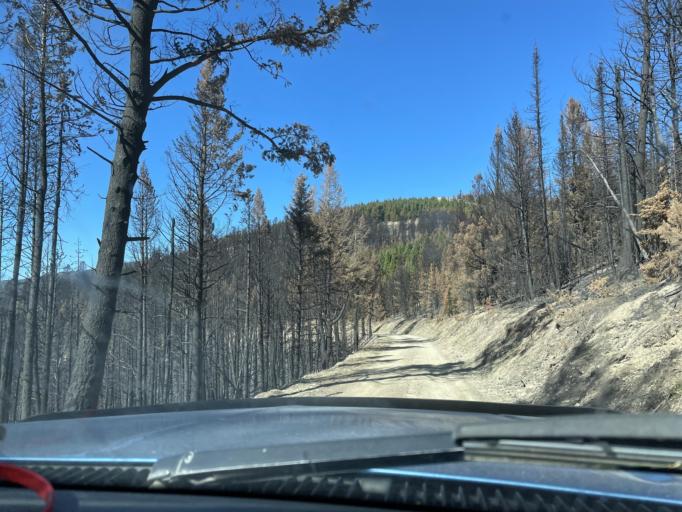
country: US
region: Montana
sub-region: Broadwater County
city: Townsend
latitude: 46.5059
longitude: -111.2755
